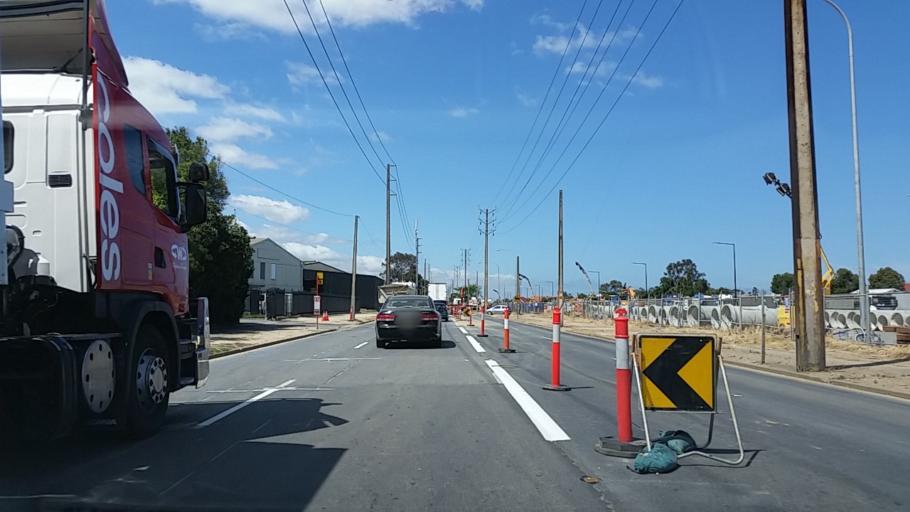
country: AU
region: South Australia
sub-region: Charles Sturt
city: Allenby Gardens
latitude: -34.8901
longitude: 138.5696
